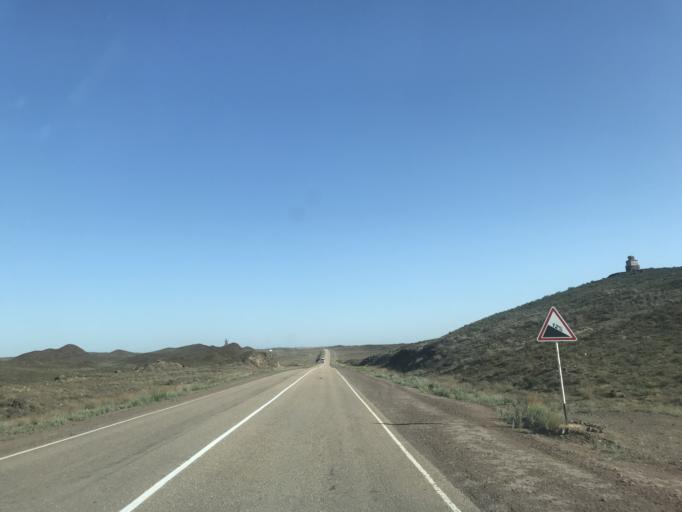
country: KZ
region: Zhambyl
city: Mynaral
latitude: 45.4173
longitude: 73.6258
